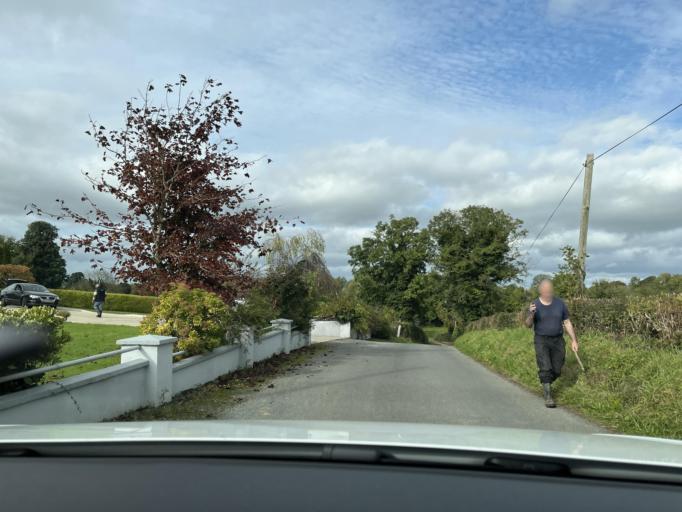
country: IE
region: Connaught
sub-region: County Leitrim
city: Carrick-on-Shannon
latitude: 53.9602
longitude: -8.0706
